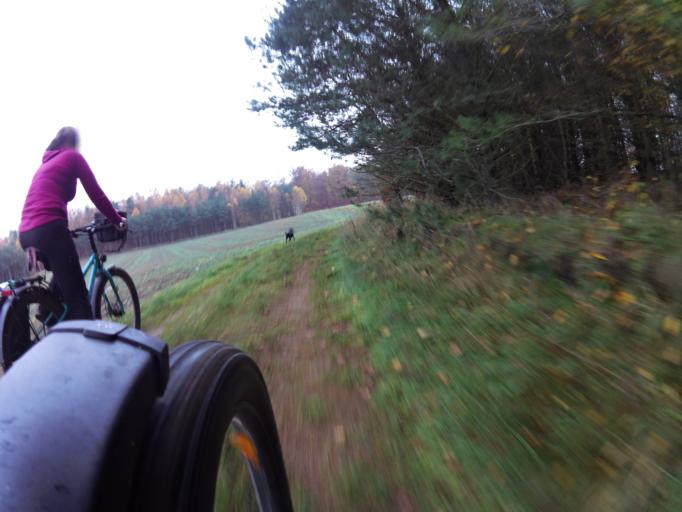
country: PL
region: Pomeranian Voivodeship
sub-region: Powiat pucki
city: Krokowa
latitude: 54.7289
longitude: 18.1316
